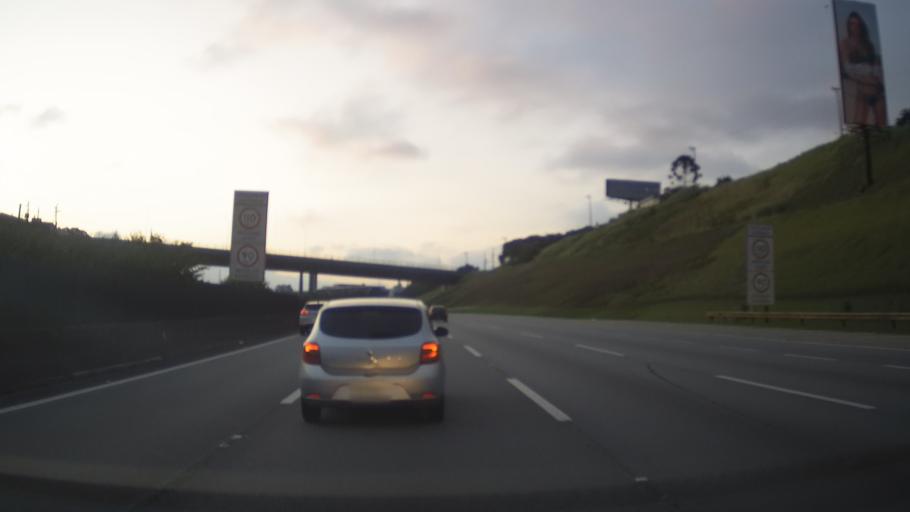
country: BR
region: Sao Paulo
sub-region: Diadema
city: Diadema
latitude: -23.6793
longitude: -46.6116
